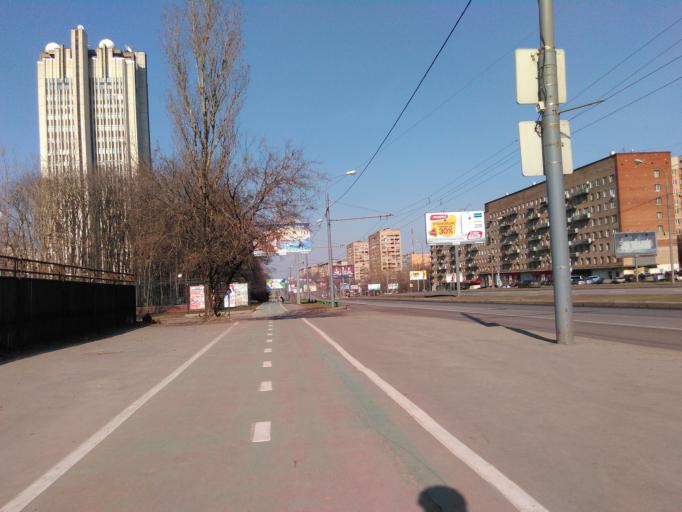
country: RU
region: Moscow
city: Ramenki
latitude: 55.6821
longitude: 37.5152
